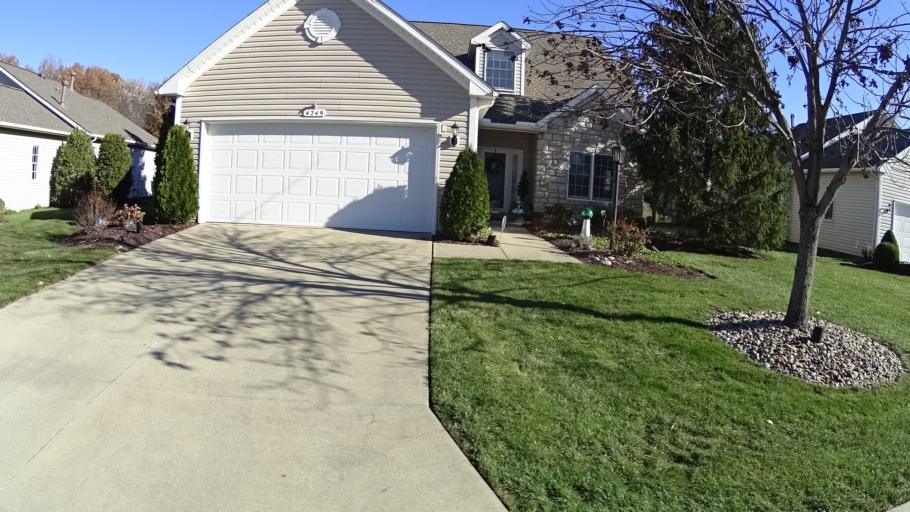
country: US
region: Ohio
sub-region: Lorain County
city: Avon Center
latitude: 41.4340
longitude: -81.9995
